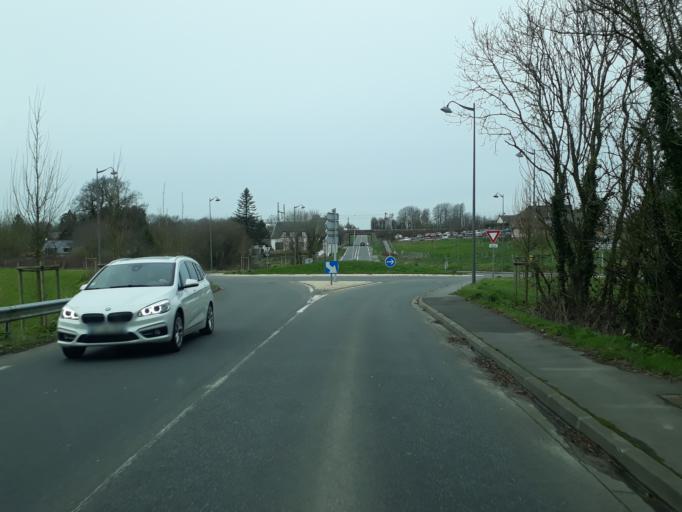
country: FR
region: Haute-Normandie
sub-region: Departement de la Seine-Maritime
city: Beuzeville-la-Grenier
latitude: 49.6008
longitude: 0.4173
